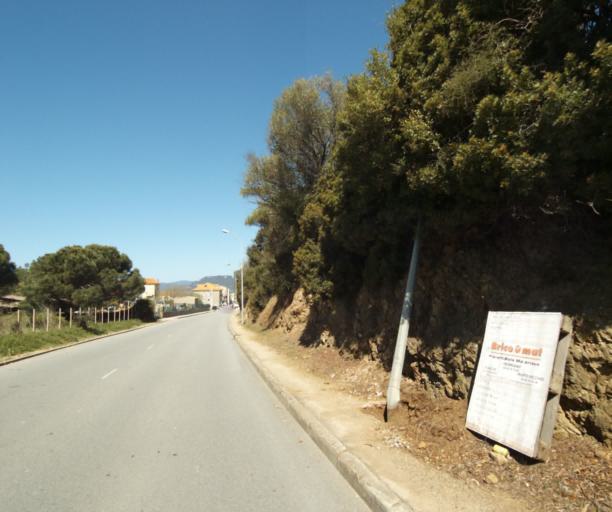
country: FR
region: Corsica
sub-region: Departement de la Corse-du-Sud
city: Propriano
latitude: 41.6727
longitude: 8.9081
